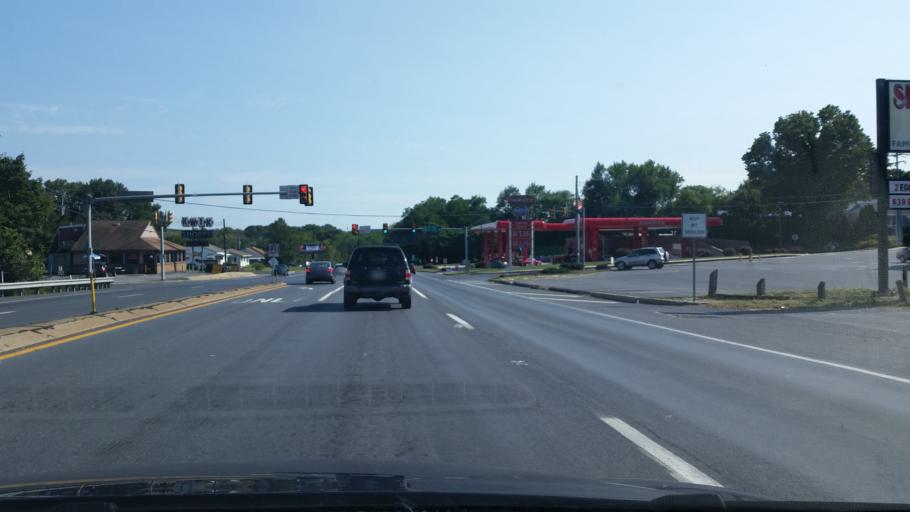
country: US
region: Pennsylvania
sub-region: Berks County
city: Shoemakersville
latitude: 40.5030
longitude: -75.9640
